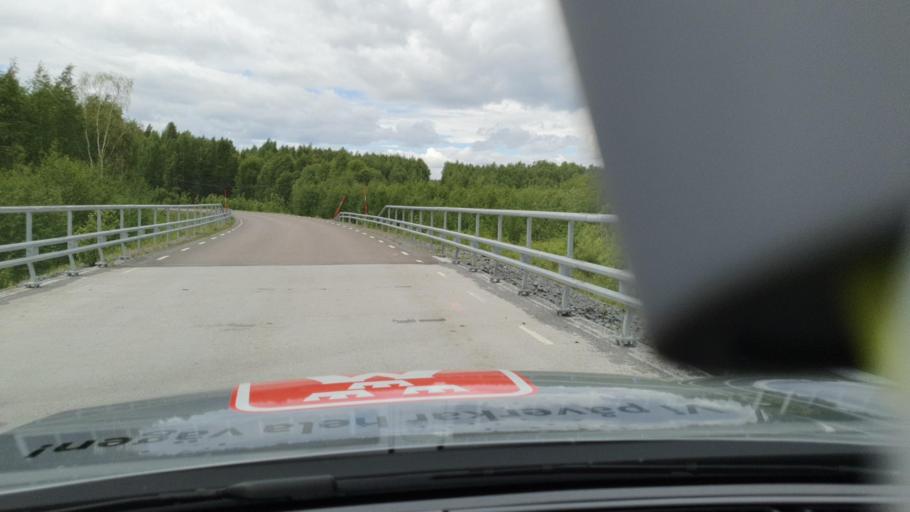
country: SE
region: Norrbotten
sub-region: Lulea Kommun
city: Sodra Sunderbyn
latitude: 65.8440
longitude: 21.9299
